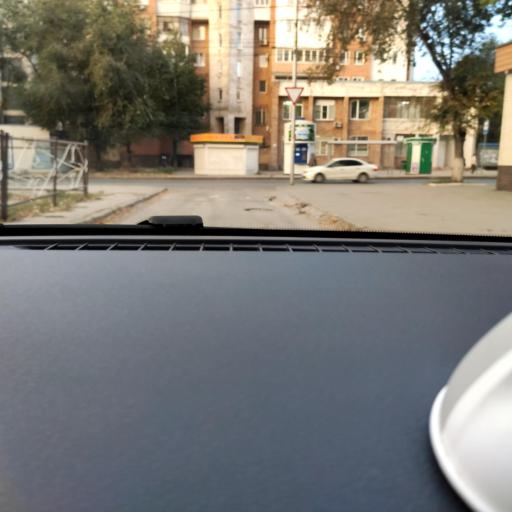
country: RU
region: Samara
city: Samara
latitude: 53.1955
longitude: 50.1376
